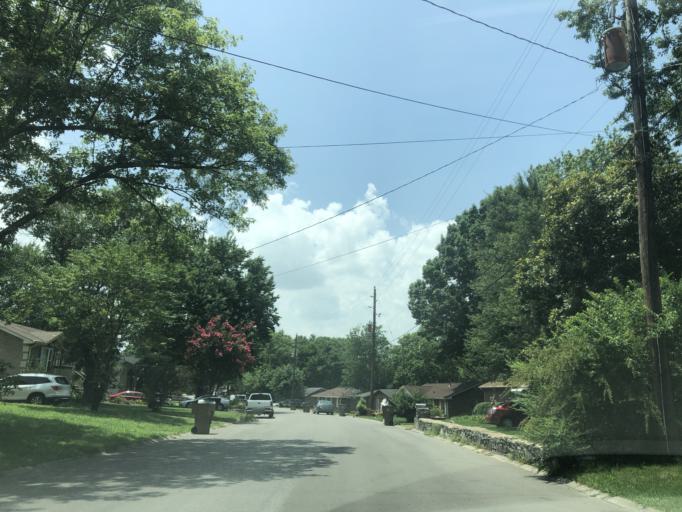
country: US
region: Tennessee
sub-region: Williamson County
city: Brentwood Estates
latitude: 36.0489
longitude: -86.6904
